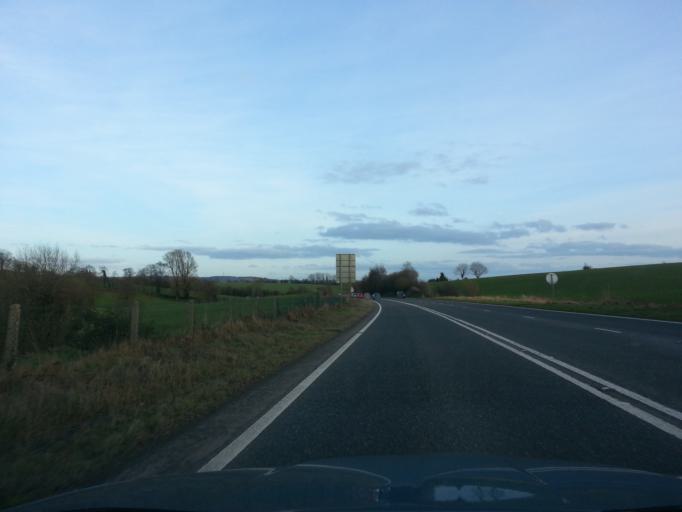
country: GB
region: Northern Ireland
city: Lisnaskea
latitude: 54.3052
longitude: -7.4883
